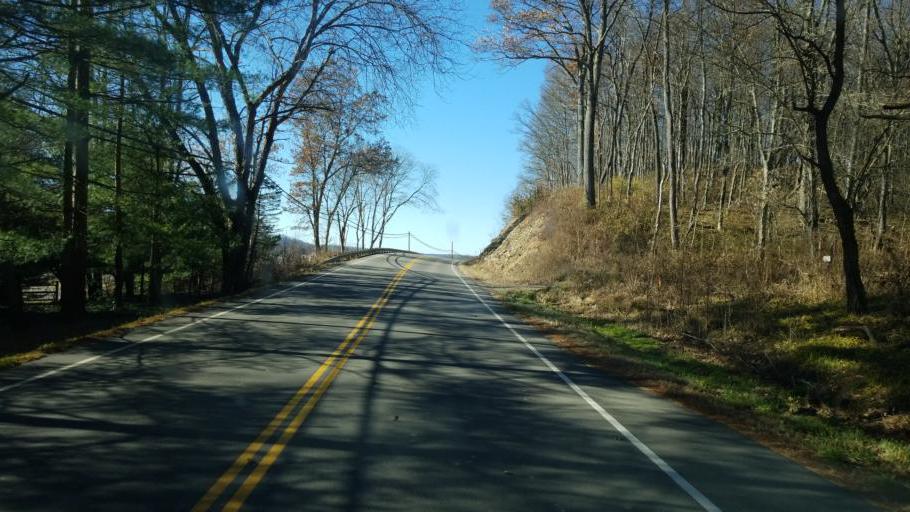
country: US
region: Ohio
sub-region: Coshocton County
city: Coshocton
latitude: 40.3407
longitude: -82.0206
